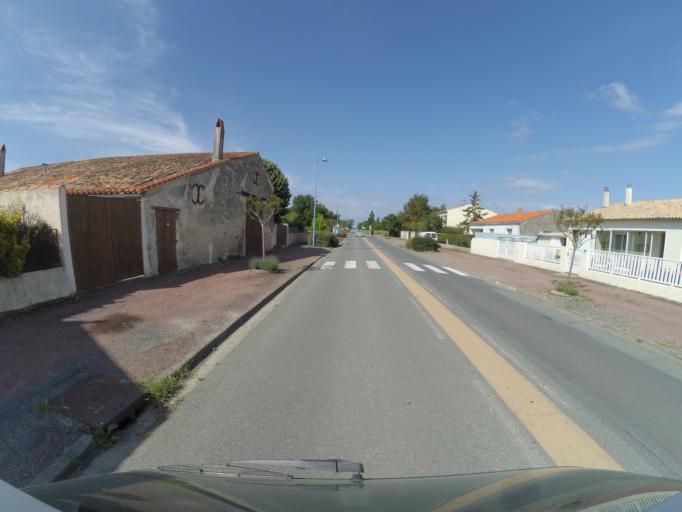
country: FR
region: Poitou-Charentes
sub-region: Departement de la Charente-Maritime
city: Andilly
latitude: 46.2441
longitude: -1.0644
